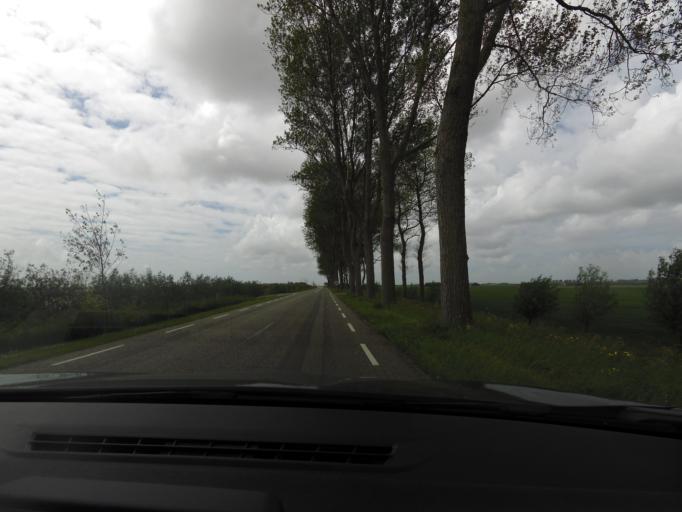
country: NL
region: South Holland
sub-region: Gemeente Goeree-Overflakkee
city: Ouddorp
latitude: 51.7135
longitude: 3.9430
